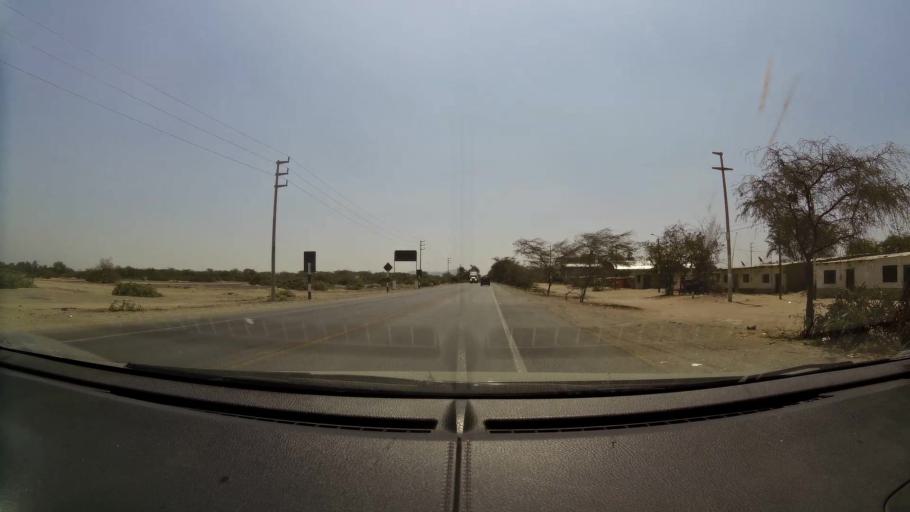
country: PE
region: Lambayeque
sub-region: Provincia de Chiclayo
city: Mocupe
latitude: -7.0183
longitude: -79.6046
